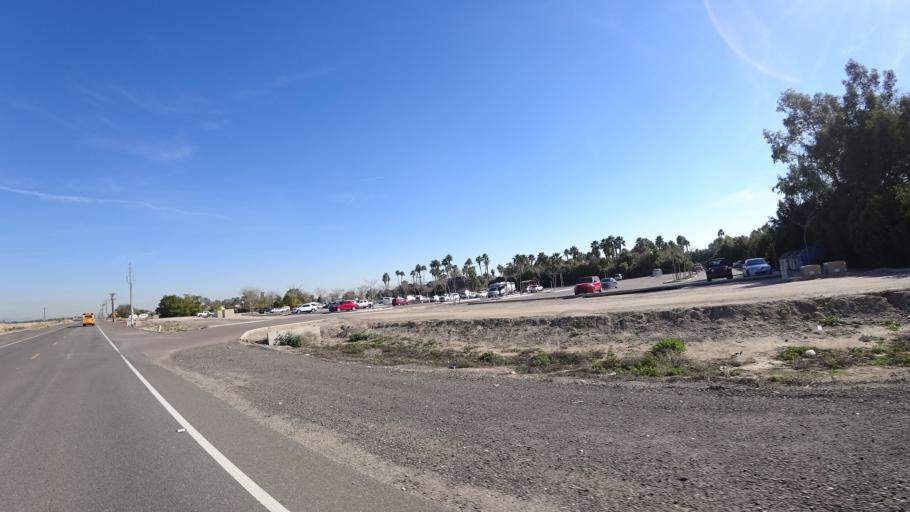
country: US
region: Arizona
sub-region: Maricopa County
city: Citrus Park
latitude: 33.5517
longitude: -112.4129
